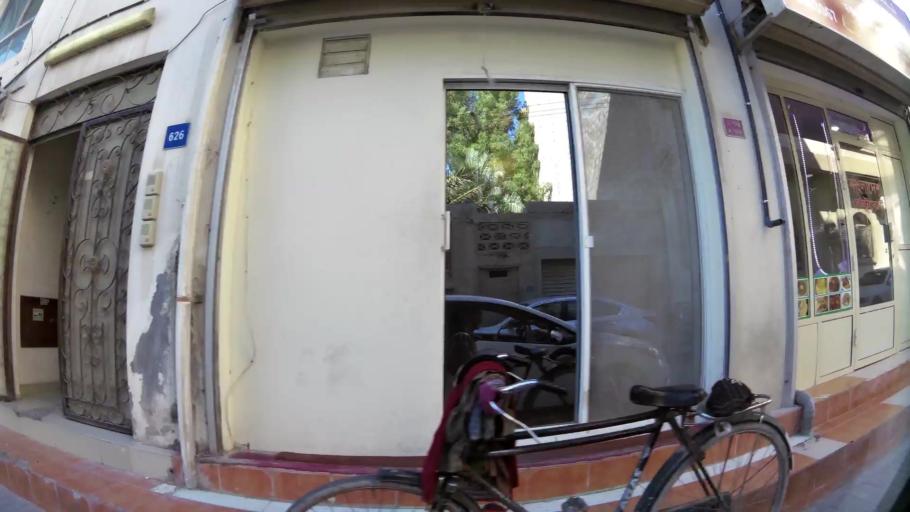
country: BH
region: Muharraq
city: Al Hadd
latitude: 26.2384
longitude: 50.6541
